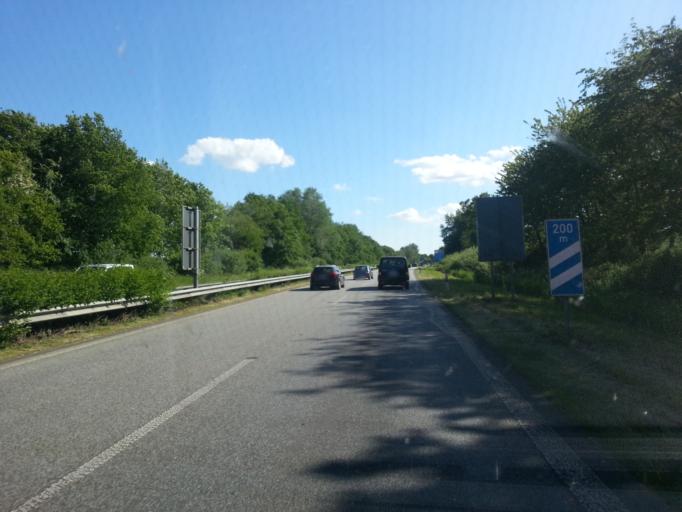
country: DE
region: Schleswig-Holstein
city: Sierksdorf
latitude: 54.0999
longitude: 10.7795
